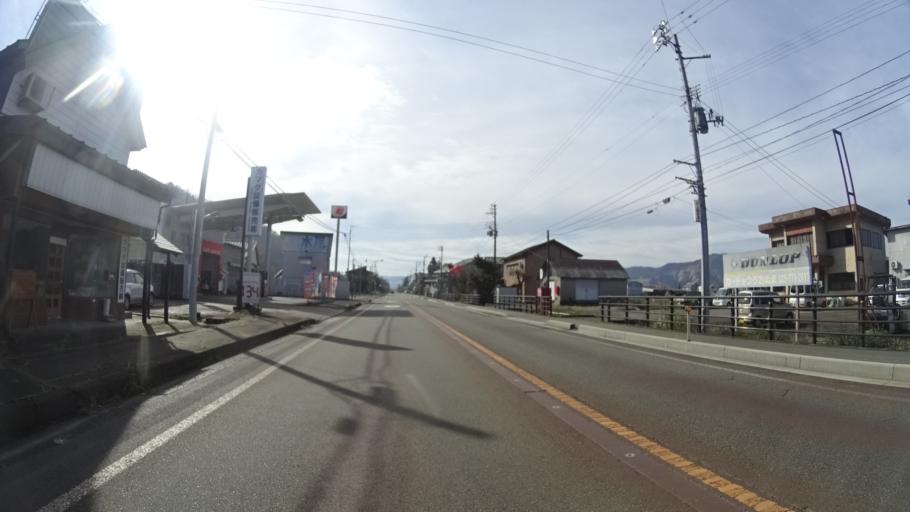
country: JP
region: Niigata
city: Muikamachi
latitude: 37.1242
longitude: 138.9300
